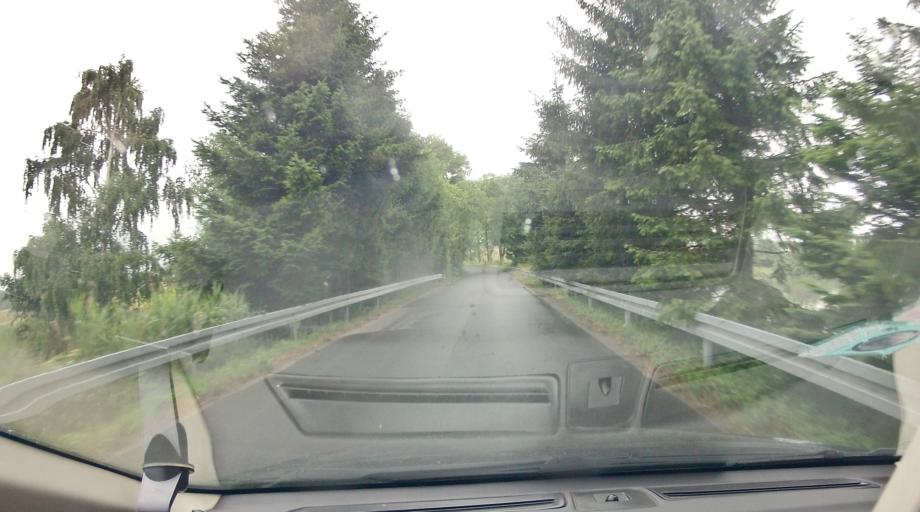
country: PL
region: Lower Silesian Voivodeship
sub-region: Powiat klodzki
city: Miedzylesie
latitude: 50.1574
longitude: 16.6836
